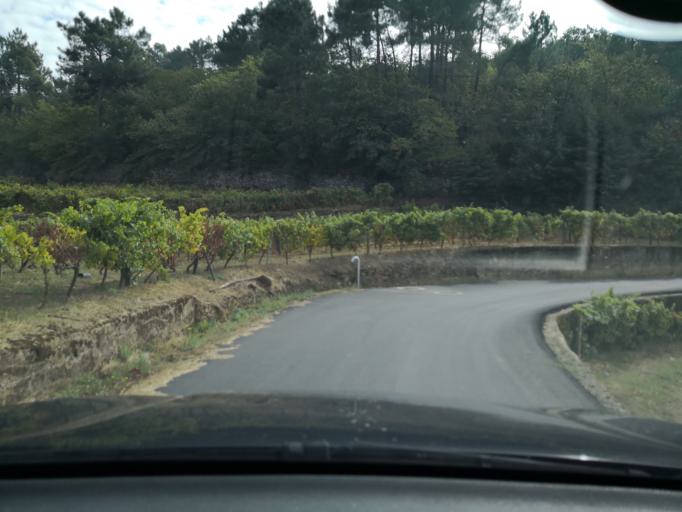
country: PT
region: Vila Real
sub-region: Sabrosa
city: Vilela
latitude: 41.2146
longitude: -7.6831
